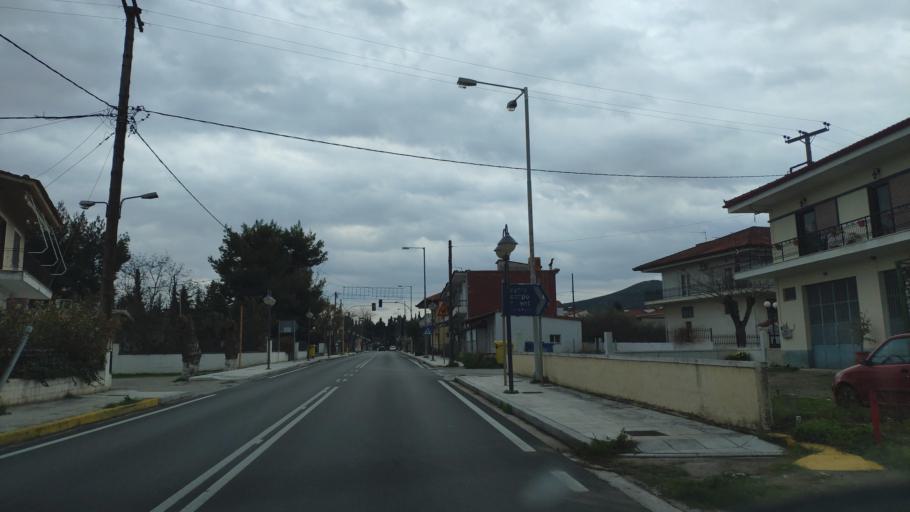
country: GR
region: Central Greece
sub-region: Nomos Voiotias
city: Livadeia
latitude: 38.4970
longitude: 22.8435
